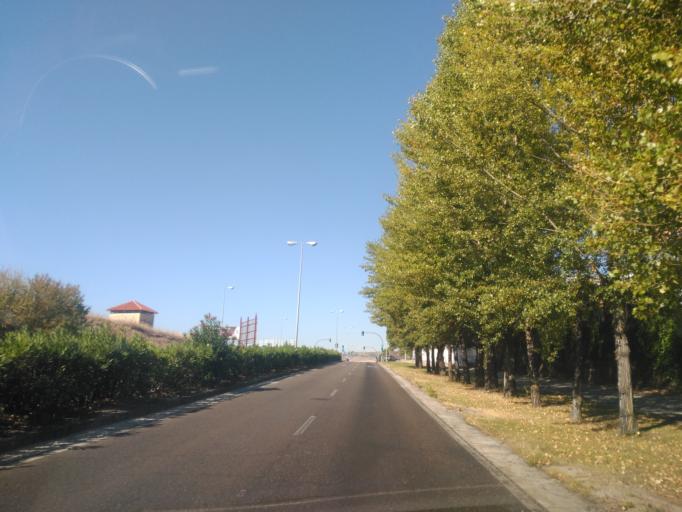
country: ES
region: Castille and Leon
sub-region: Provincia de Valladolid
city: Zaratan
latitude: 41.6312
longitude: -4.7645
